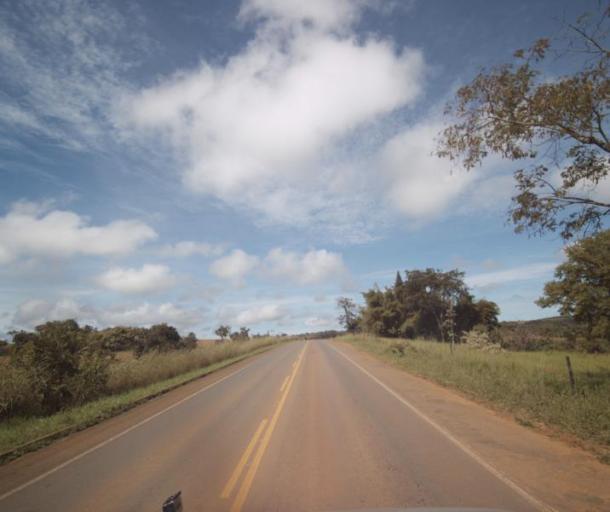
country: BR
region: Goias
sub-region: Pirenopolis
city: Pirenopolis
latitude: -15.9981
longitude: -48.8392
